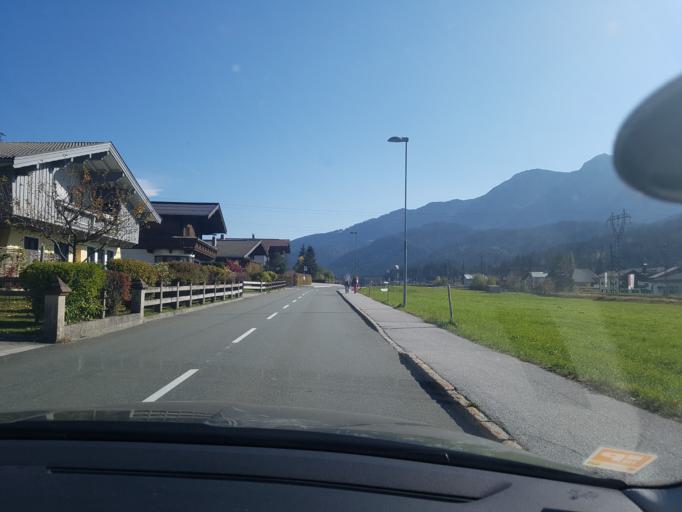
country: AT
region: Tyrol
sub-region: Politischer Bezirk Kitzbuhel
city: Hochfilzen
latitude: 47.4717
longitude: 12.6221
